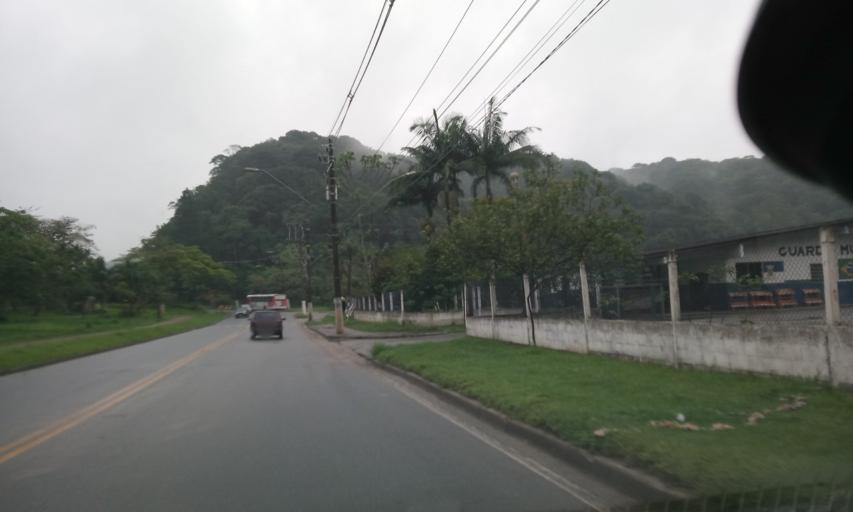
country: BR
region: Sao Paulo
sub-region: Maua
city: Maua
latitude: -23.7308
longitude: -46.4956
